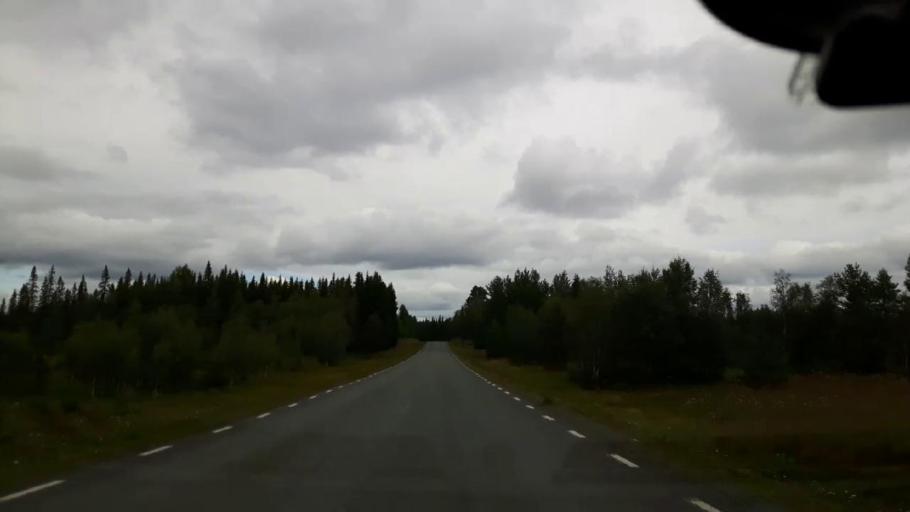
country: SE
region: Jaemtland
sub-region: Krokoms Kommun
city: Valla
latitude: 63.5532
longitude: 13.8503
